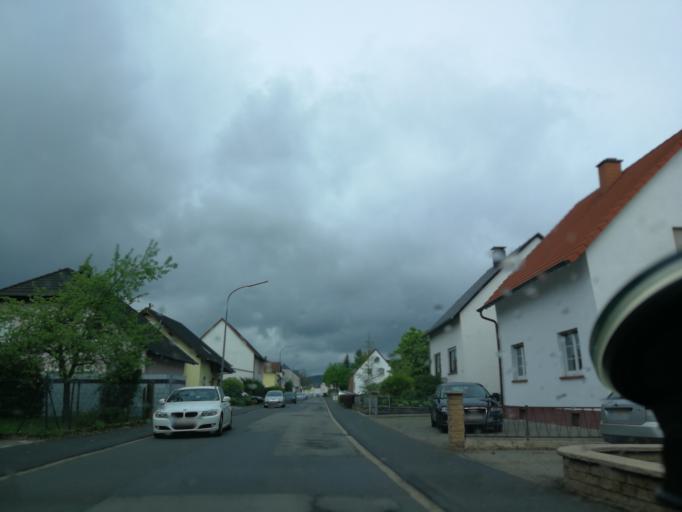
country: DE
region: Rheinland-Pfalz
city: Neuerburg
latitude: 49.9799
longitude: 6.9444
